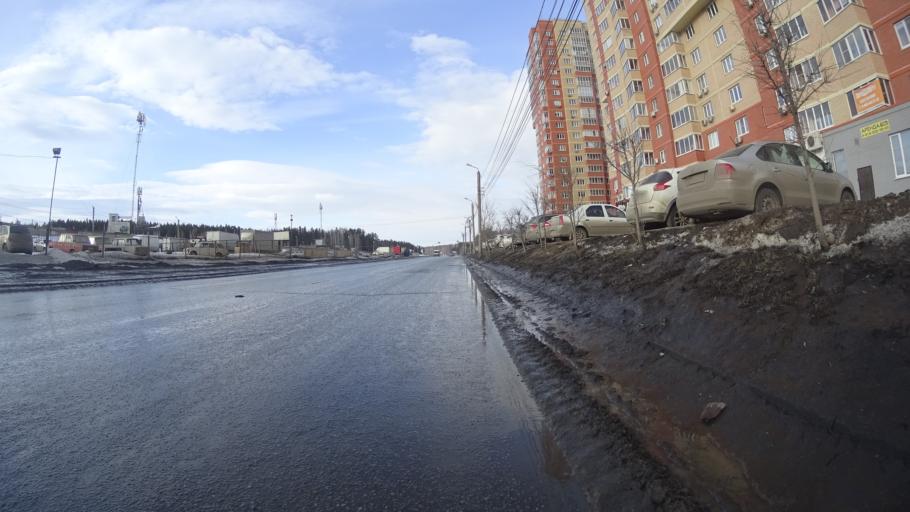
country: RU
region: Chelyabinsk
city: Roshchino
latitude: 55.1943
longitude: 61.2802
